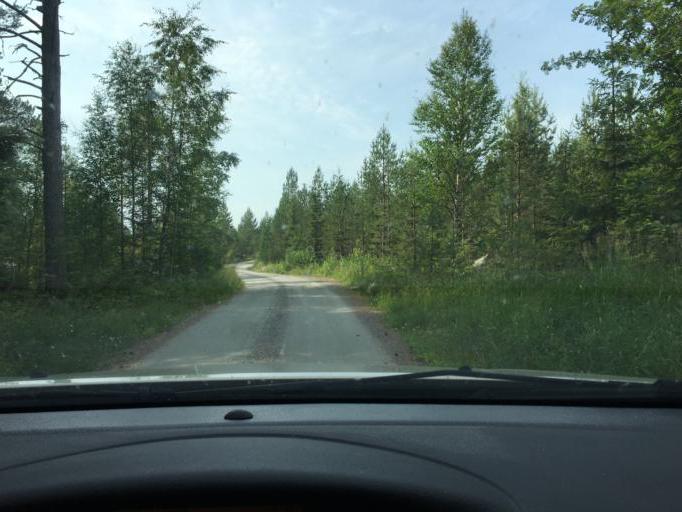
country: SE
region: Norrbotten
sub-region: Kalix Kommun
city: Rolfs
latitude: 65.7653
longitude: 23.0028
